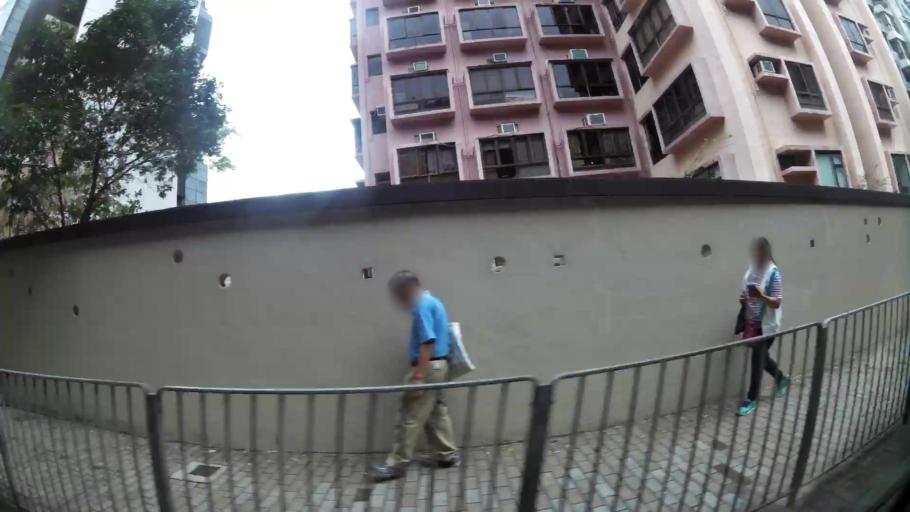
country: HK
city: Hong Kong
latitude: 22.2811
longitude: 114.1208
